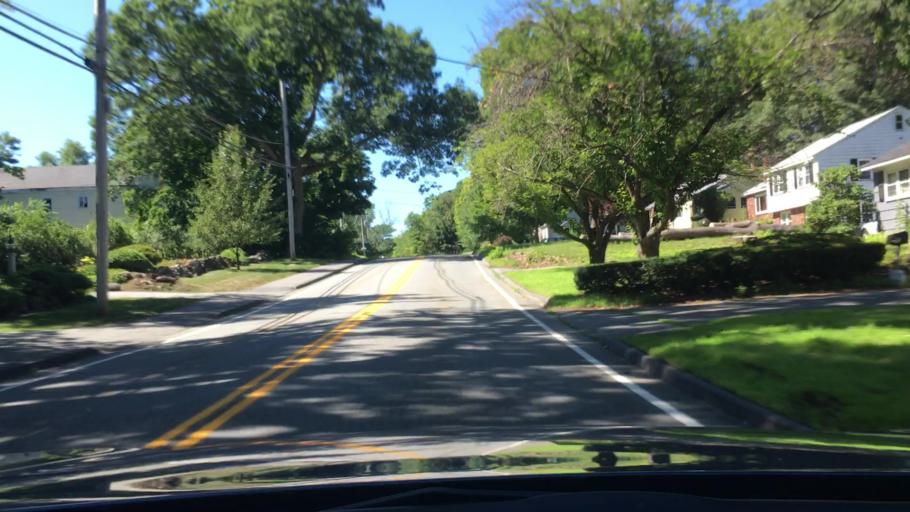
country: US
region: Massachusetts
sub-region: Middlesex County
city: Billerica
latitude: 42.5682
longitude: -71.2627
